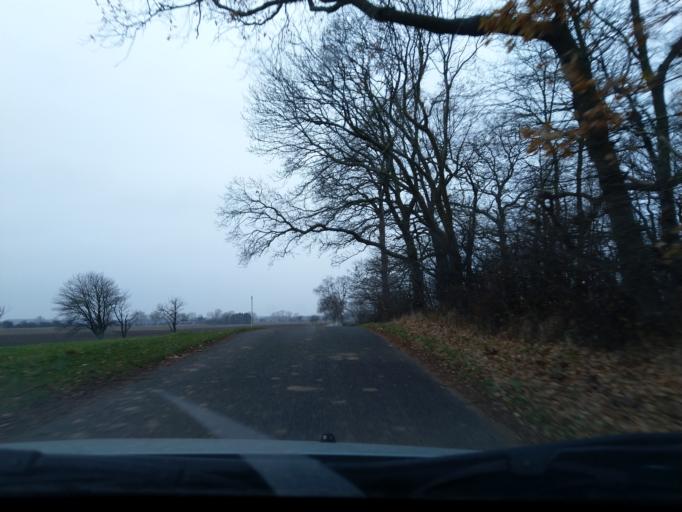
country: DK
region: Zealand
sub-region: Vordingborg Kommune
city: Praesto
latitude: 55.1146
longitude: 12.1416
